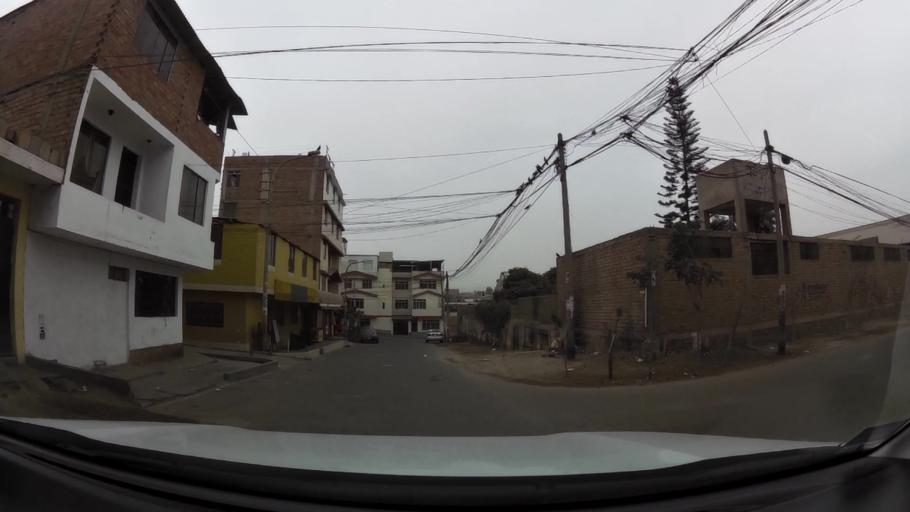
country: PE
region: Lima
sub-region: Lima
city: Surco
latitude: -12.1571
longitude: -76.9765
